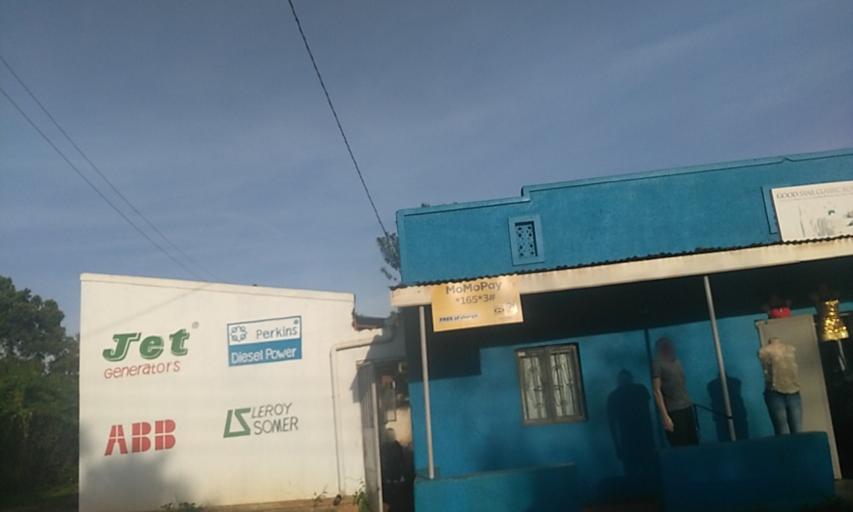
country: UG
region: Central Region
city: Kampala Central Division
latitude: 0.3636
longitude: 32.5987
